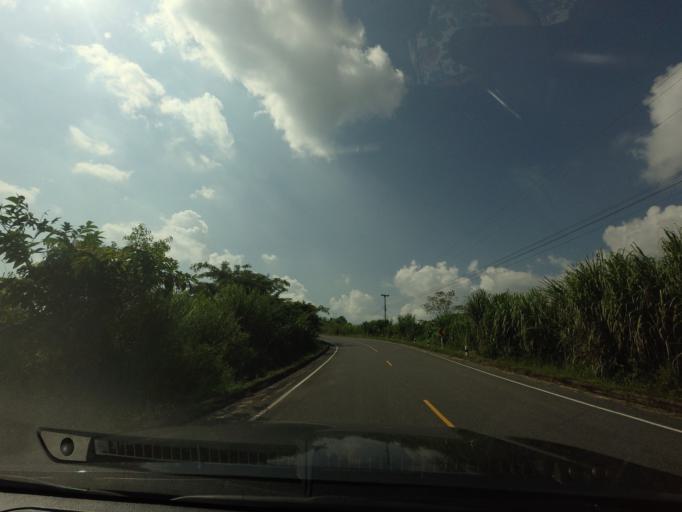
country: TH
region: Nan
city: Santi Suk
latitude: 18.9776
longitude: 101.0070
